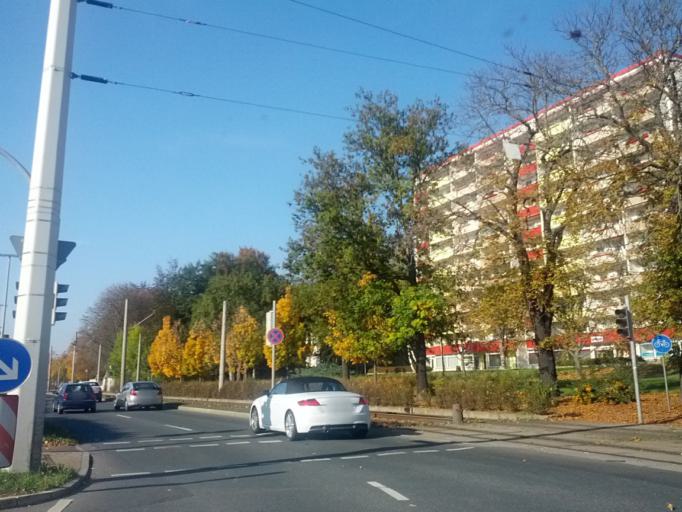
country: DE
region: Thuringia
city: Gera
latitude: 50.8942
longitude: 12.0799
